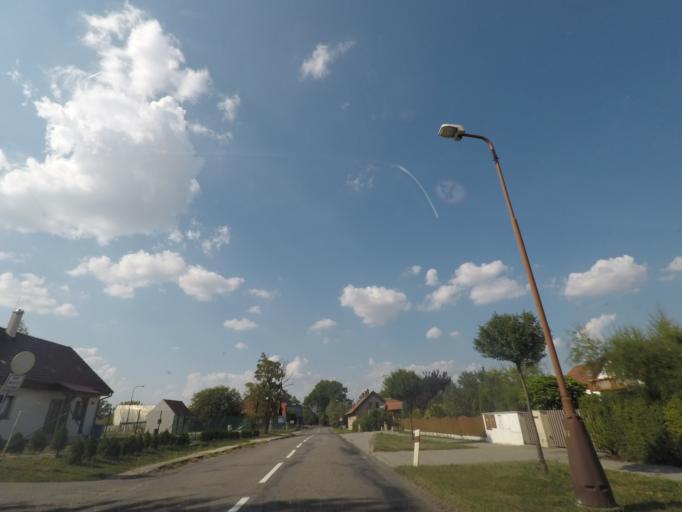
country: CZ
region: Kralovehradecky
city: Dolni Cernilov
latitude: 50.2396
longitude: 15.9673
